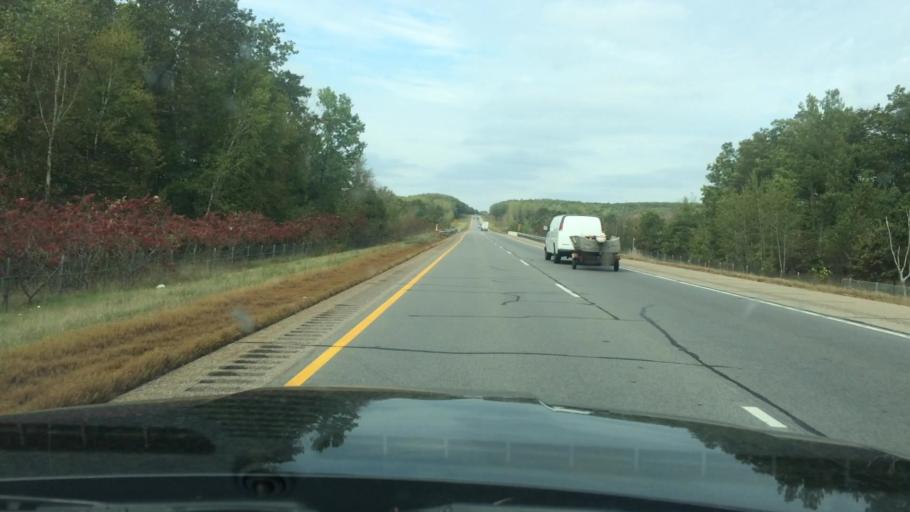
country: US
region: Wisconsin
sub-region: Marathon County
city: Mosinee
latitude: 44.6934
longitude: -89.6430
